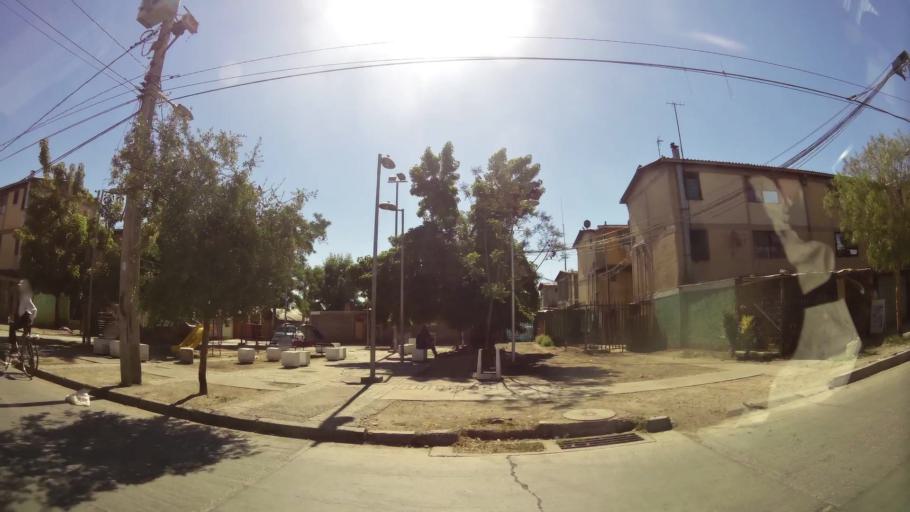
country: CL
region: Santiago Metropolitan
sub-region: Provincia de Maipo
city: San Bernardo
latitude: -33.5852
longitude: -70.6698
